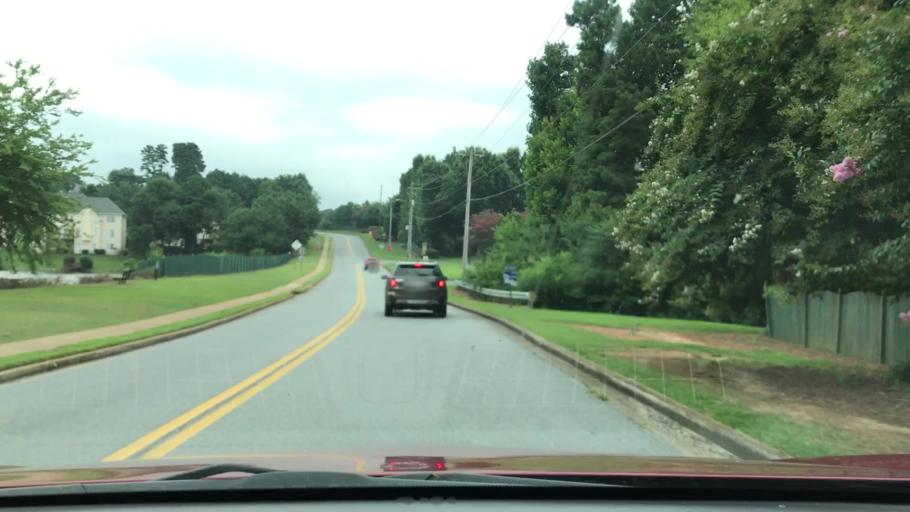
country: US
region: Georgia
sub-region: Gwinnett County
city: Suwanee
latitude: 34.0063
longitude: -84.0275
